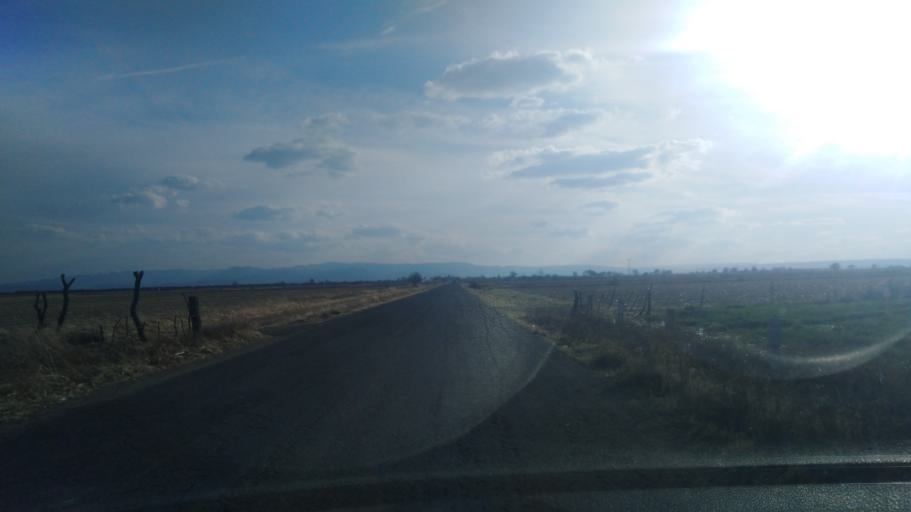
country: MX
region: Durango
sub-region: Durango
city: Jose Refugio Salcido
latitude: 24.0108
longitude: -104.4683
